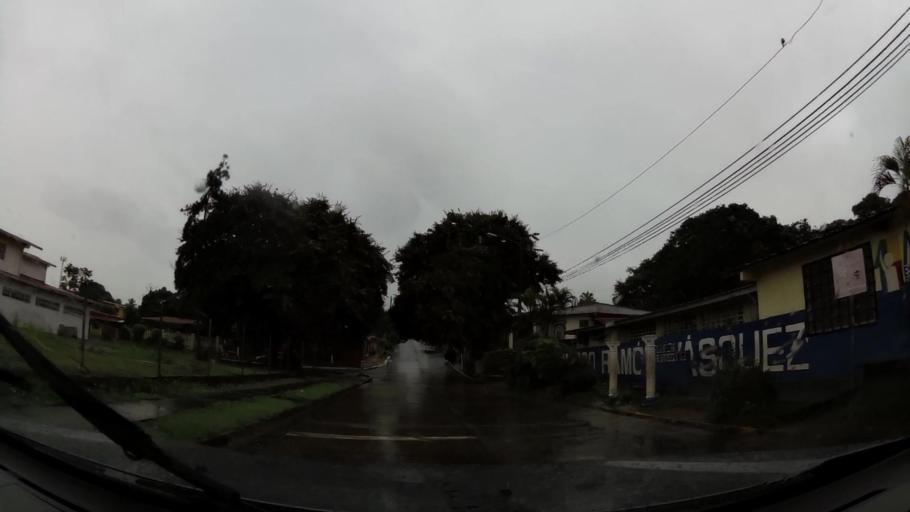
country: PA
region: Colon
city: Sabanitas
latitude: 9.3430
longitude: -79.8077
